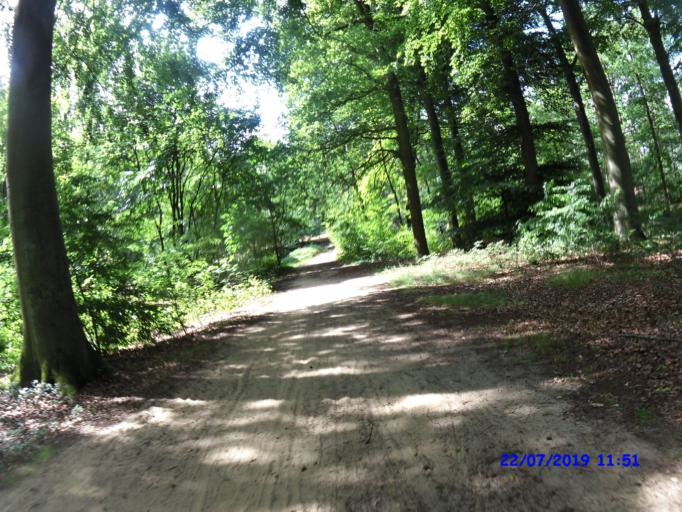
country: BE
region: Flanders
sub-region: Provincie Antwerpen
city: Westerlo
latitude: 51.0861
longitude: 4.8964
